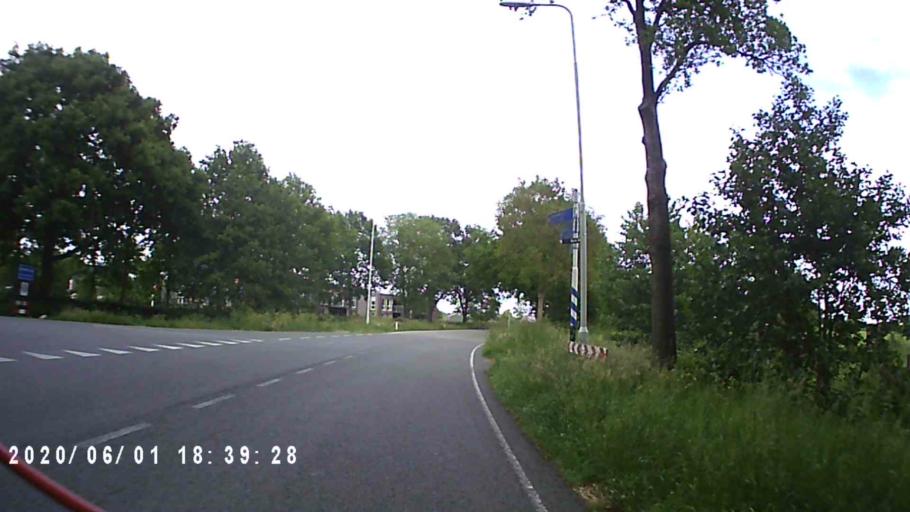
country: NL
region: Friesland
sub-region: Gemeente Tytsjerksteradiel
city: Eastermar
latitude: 53.1740
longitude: 6.0621
